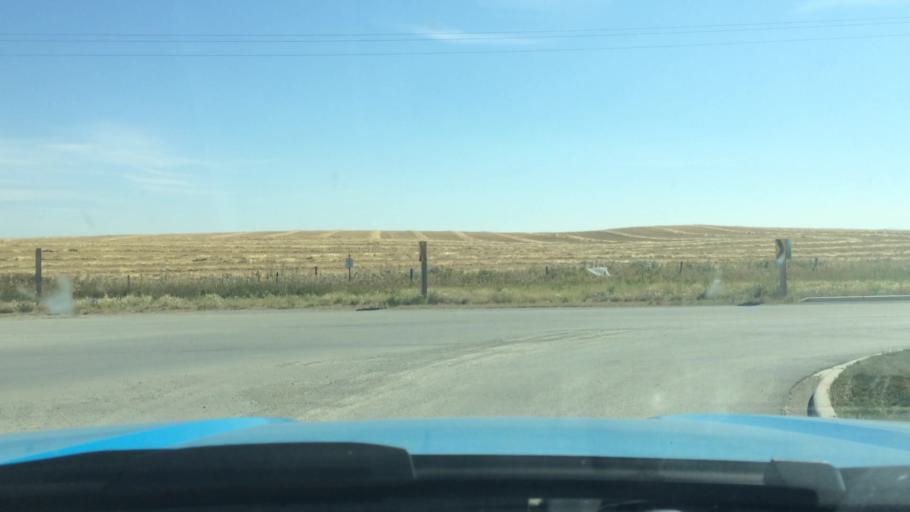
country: CA
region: Alberta
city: Airdrie
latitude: 51.2172
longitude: -113.9355
